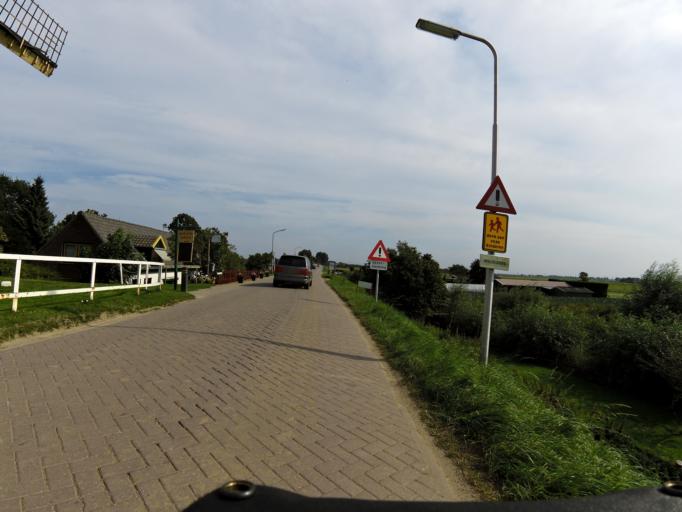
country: NL
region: South Holland
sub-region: Gemeente Zwijndrecht
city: Heerjansdam
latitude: 51.8026
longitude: 4.5748
